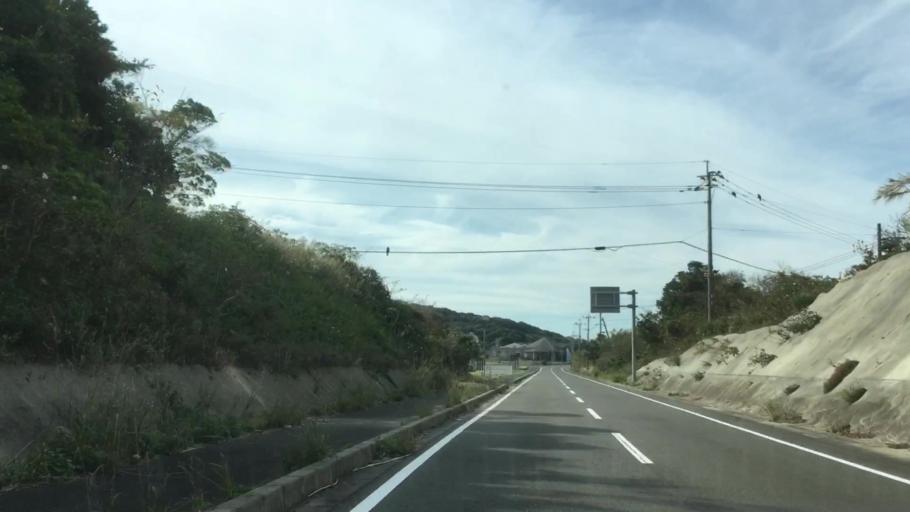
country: JP
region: Nagasaki
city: Sasebo
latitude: 33.0183
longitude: 129.5743
